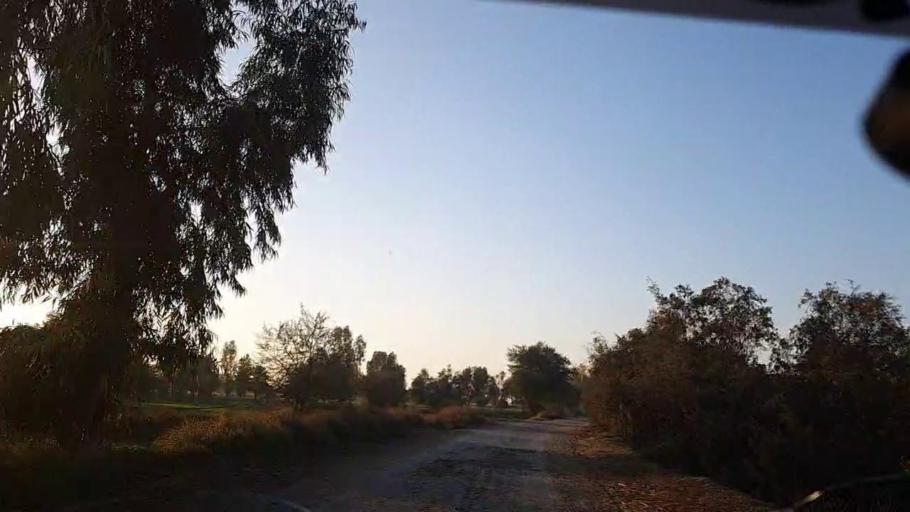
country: PK
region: Sindh
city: Khanpur
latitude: 27.8180
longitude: 69.3003
